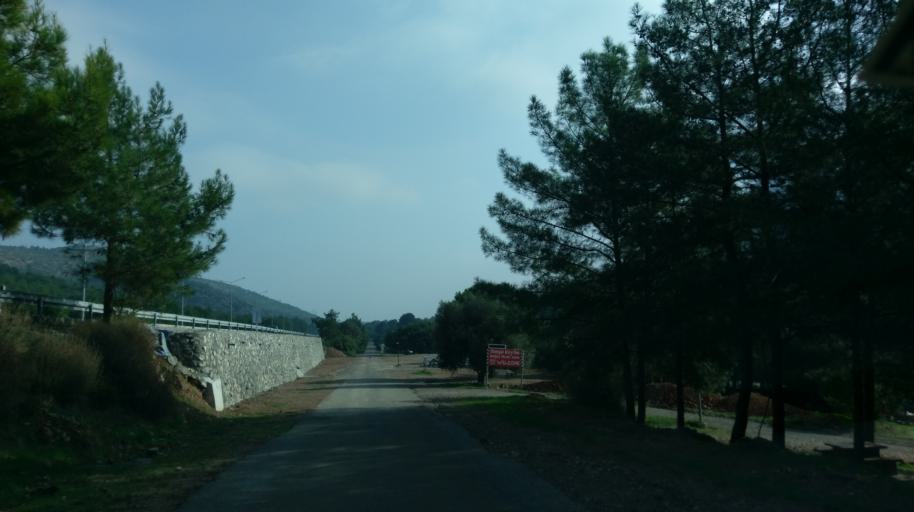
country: CY
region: Keryneia
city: Kyrenia
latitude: 35.3024
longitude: 33.2914
